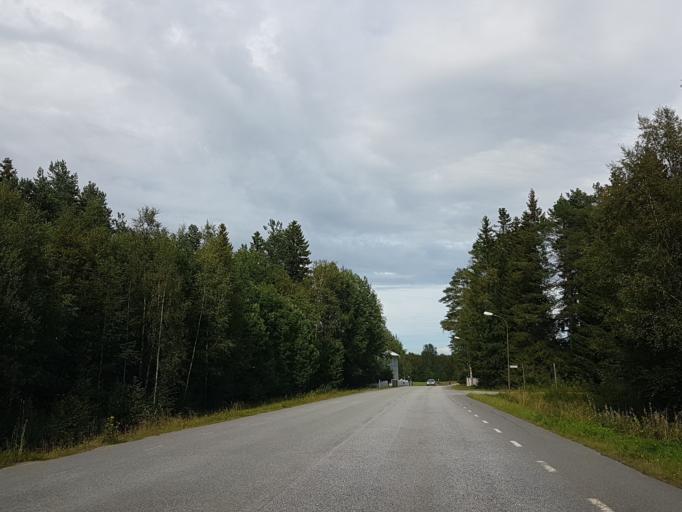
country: SE
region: Vaesterbotten
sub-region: Umea Kommun
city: Taftea
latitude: 63.8352
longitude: 20.4744
